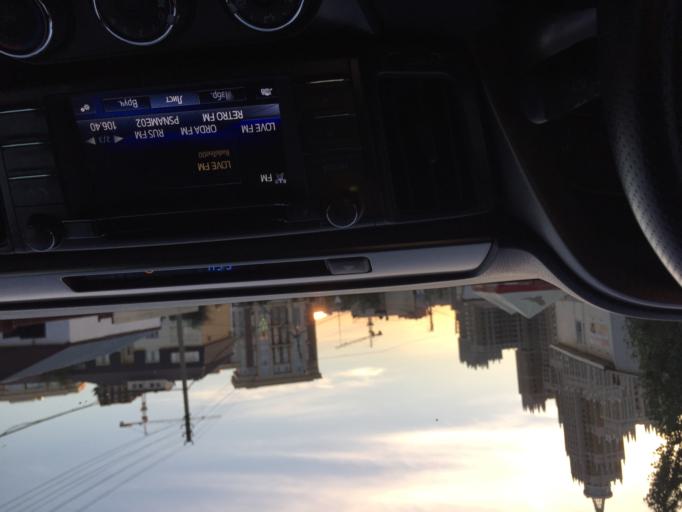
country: KZ
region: Astana Qalasy
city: Astana
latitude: 51.1400
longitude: 71.4201
